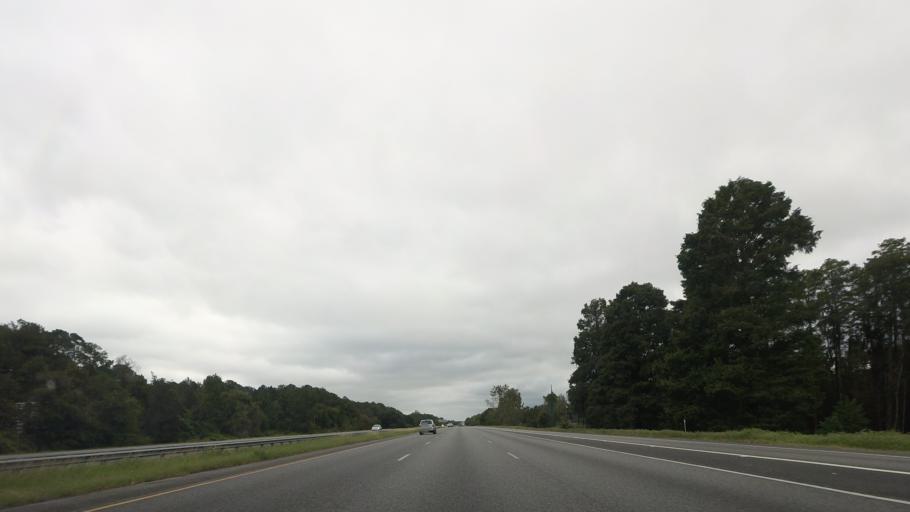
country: US
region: Georgia
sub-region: Echols County
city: Statenville
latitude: 30.6411
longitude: -83.1870
